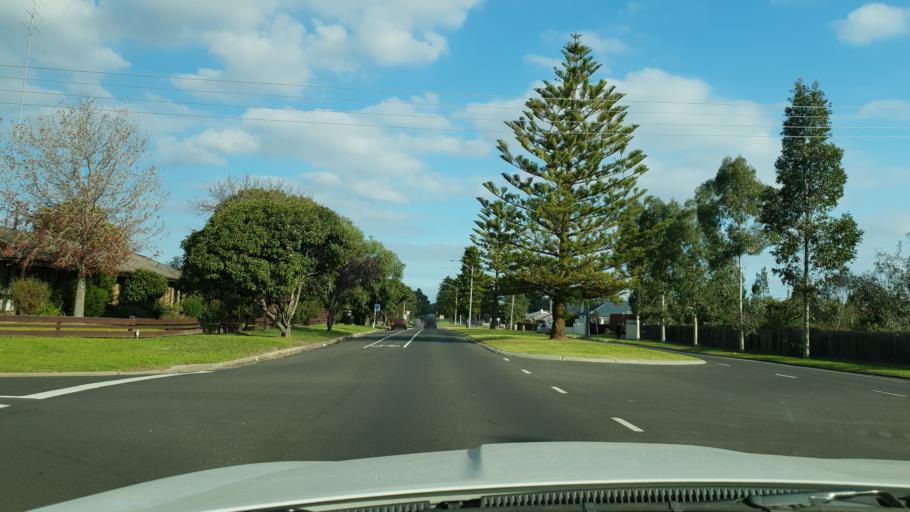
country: AU
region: Victoria
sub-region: East Gippsland
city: Bairnsdale
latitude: -37.8175
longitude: 147.6088
